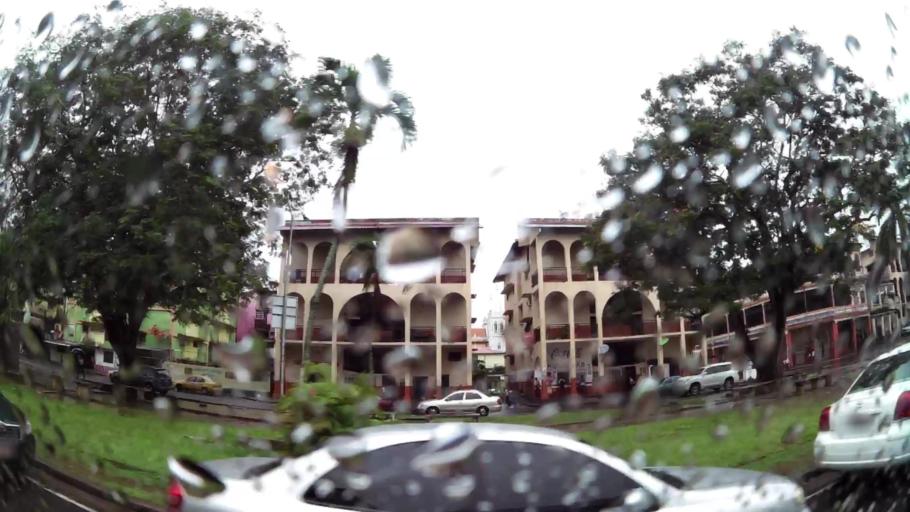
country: PA
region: Colon
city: Colon
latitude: 9.3613
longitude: -79.9026
